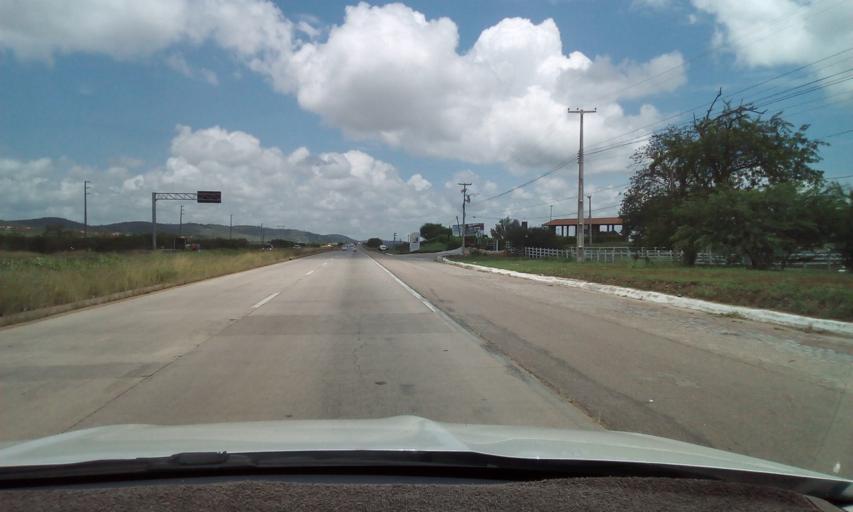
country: BR
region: Pernambuco
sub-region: Gravata
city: Gravata
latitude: -8.2107
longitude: -35.6145
